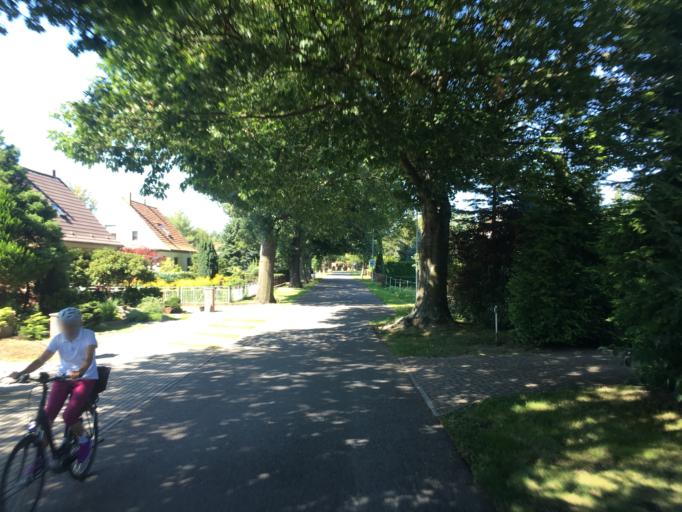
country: DE
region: Brandenburg
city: Welzow
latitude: 51.5200
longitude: 14.1761
